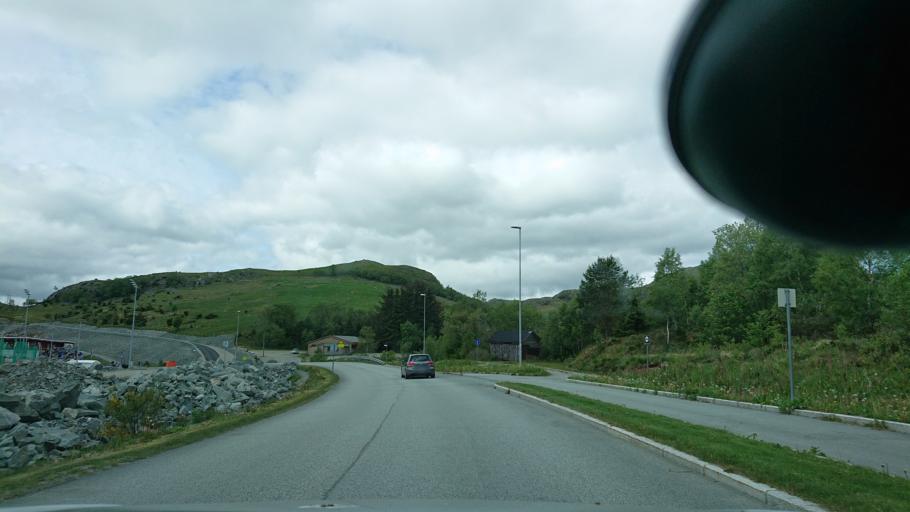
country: NO
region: Rogaland
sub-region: Gjesdal
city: Algard
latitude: 58.7764
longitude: 5.8686
